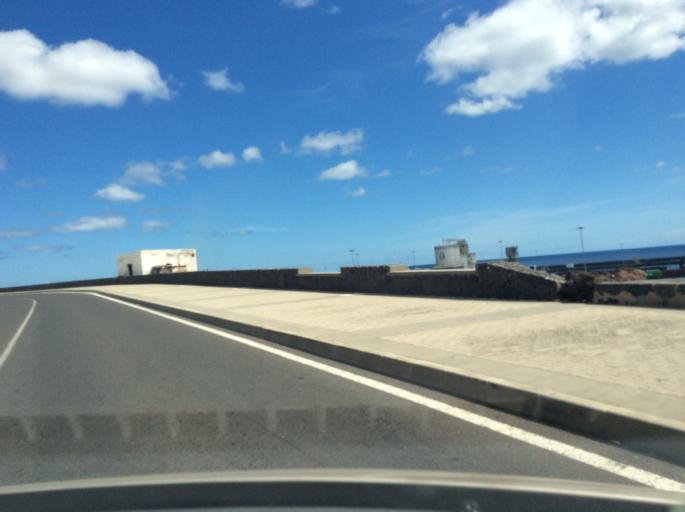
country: ES
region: Canary Islands
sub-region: Provincia de Las Palmas
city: Arrecife
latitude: 28.9721
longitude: -13.5333
